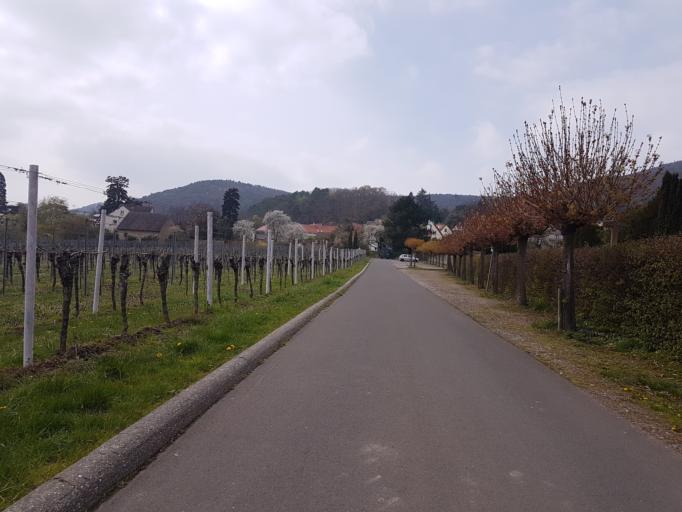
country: DE
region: Rheinland-Pfalz
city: Gleisweiler
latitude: 49.2431
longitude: 8.0698
